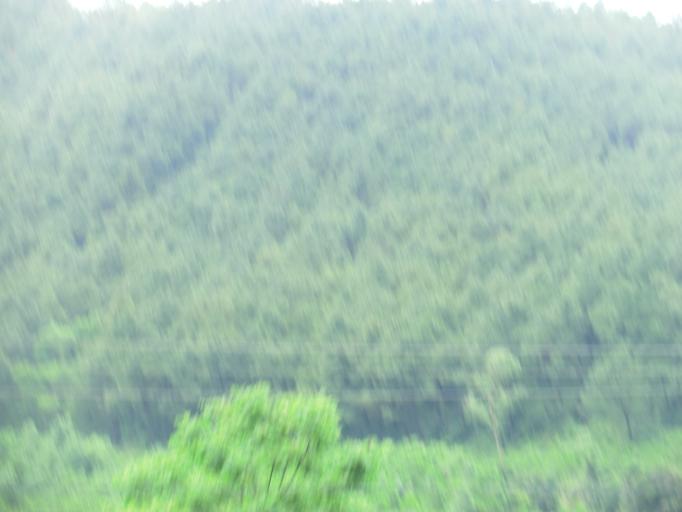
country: VN
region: Thua Thien-Hue
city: Phu Loc
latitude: 16.2813
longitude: 107.9110
